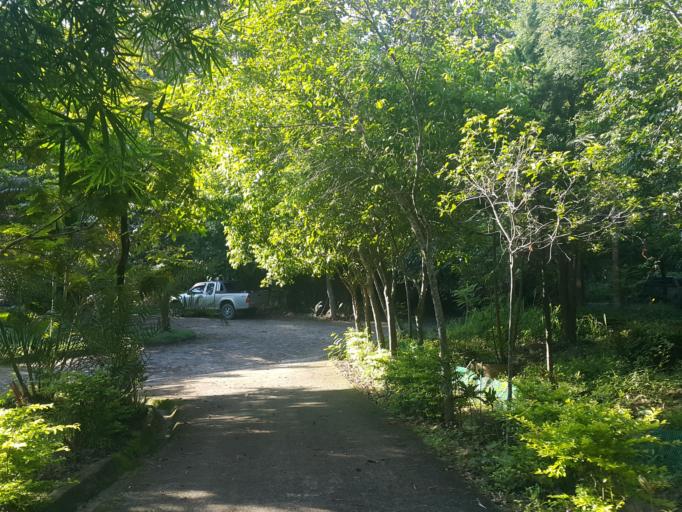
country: TH
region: Chiang Mai
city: Mae On
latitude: 18.7030
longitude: 99.2082
